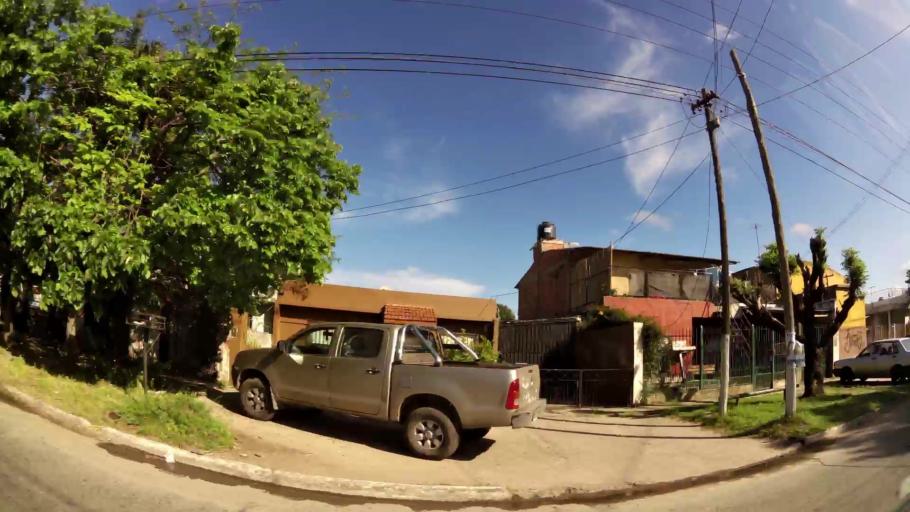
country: AR
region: Buenos Aires
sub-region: Partido de Quilmes
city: Quilmes
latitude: -34.7959
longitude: -58.2296
